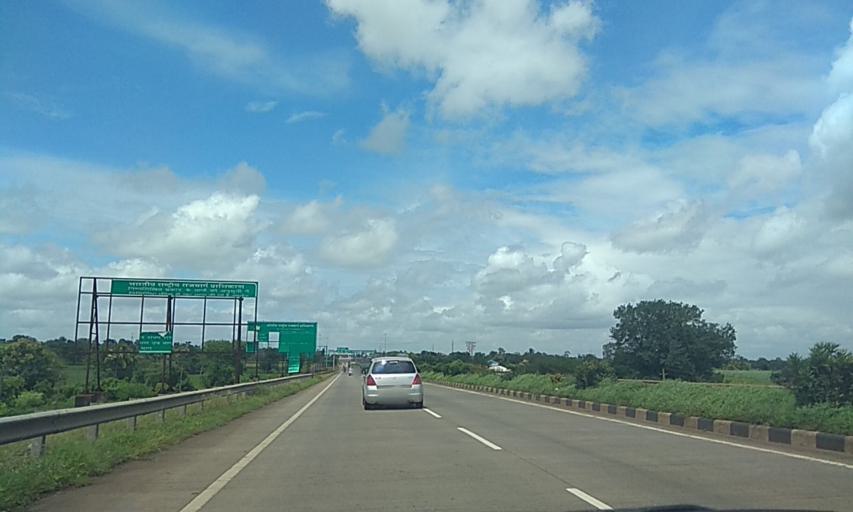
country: IN
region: Karnataka
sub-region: Belgaum
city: Sankeshwar
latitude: 16.1364
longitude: 74.5165
